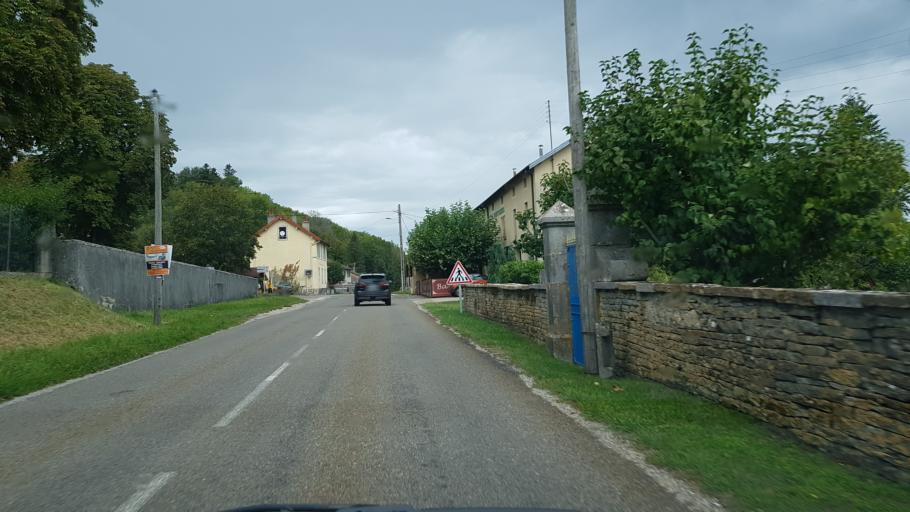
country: FR
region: Rhone-Alpes
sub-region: Departement de l'Ain
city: Cuisiat
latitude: 46.3288
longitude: 5.4377
